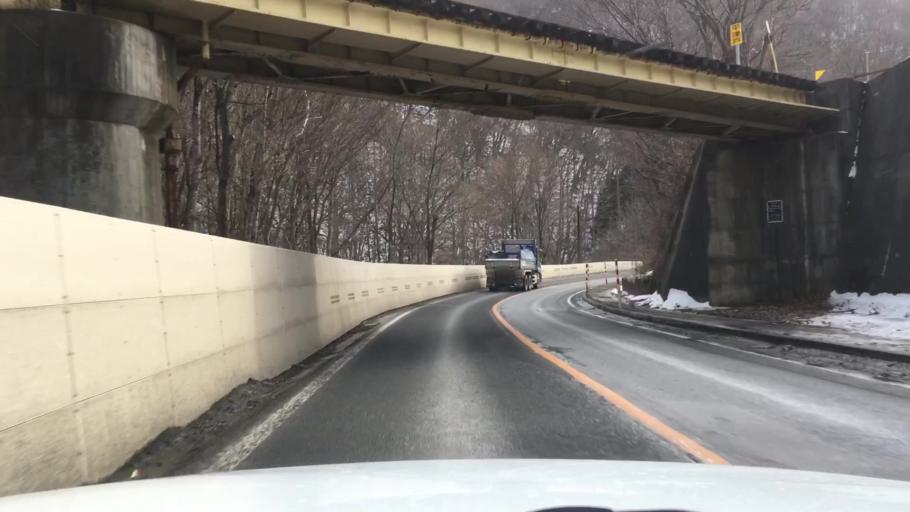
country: JP
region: Iwate
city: Tono
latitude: 39.6248
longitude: 141.5139
